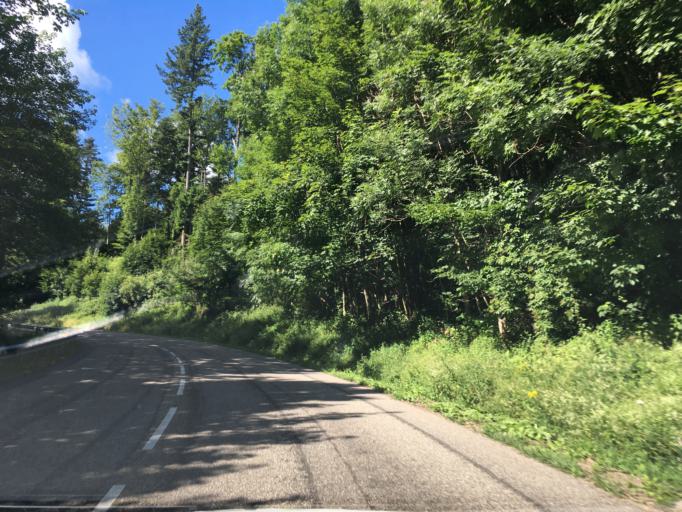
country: FR
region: Alsace
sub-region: Departement du Haut-Rhin
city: Sainte-Marie-aux-Mines
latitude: 48.2484
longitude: 7.1455
